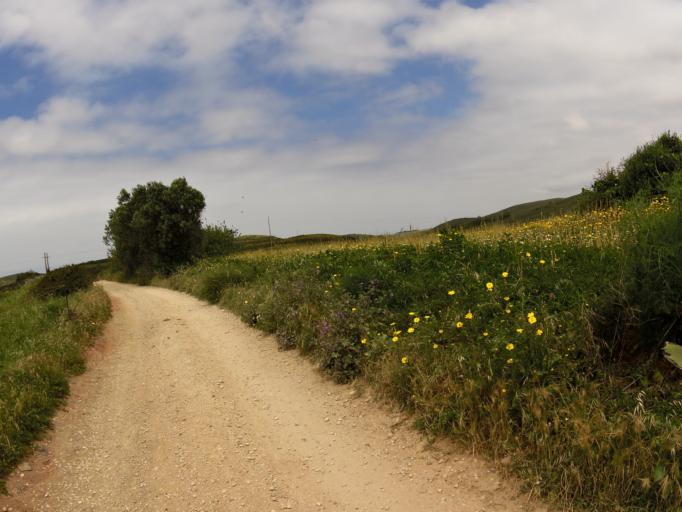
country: PT
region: Faro
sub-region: Vila do Bispo
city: Vila do Bispo
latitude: 37.0849
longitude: -8.8922
